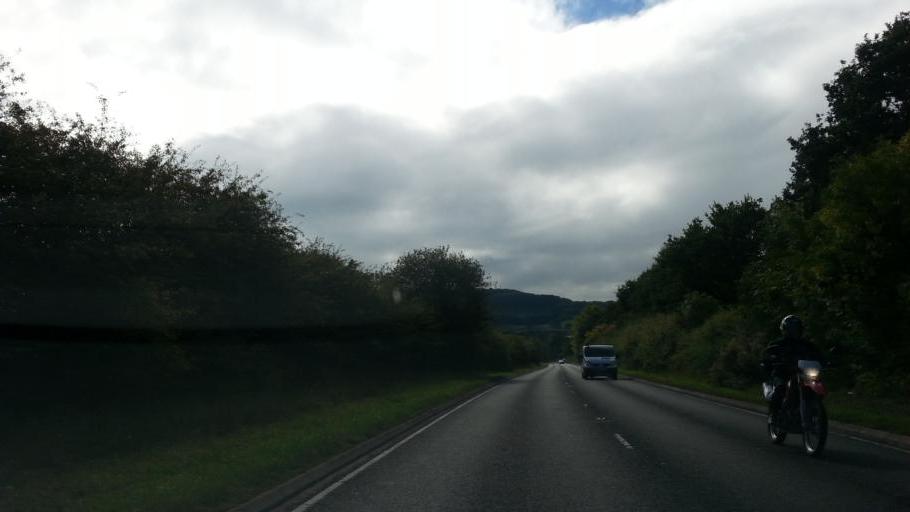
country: GB
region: England
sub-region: Herefordshire
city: Ross on Wye
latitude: 51.9247
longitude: -2.5709
